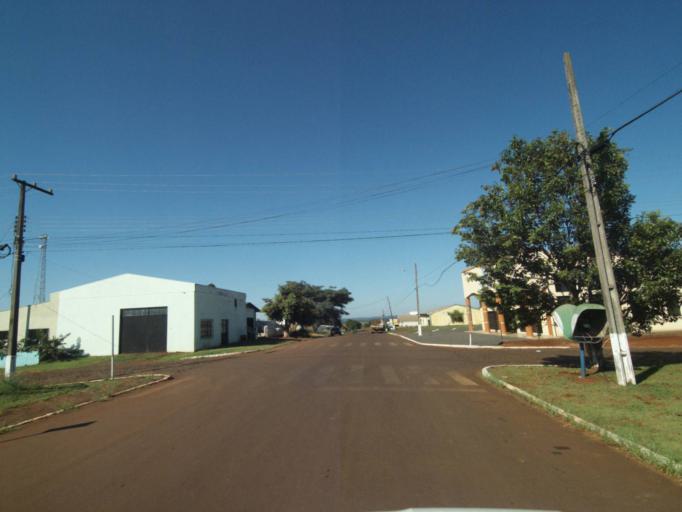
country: BR
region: Parana
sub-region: Laranjeiras Do Sul
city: Laranjeiras do Sul
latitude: -25.4933
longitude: -52.5327
